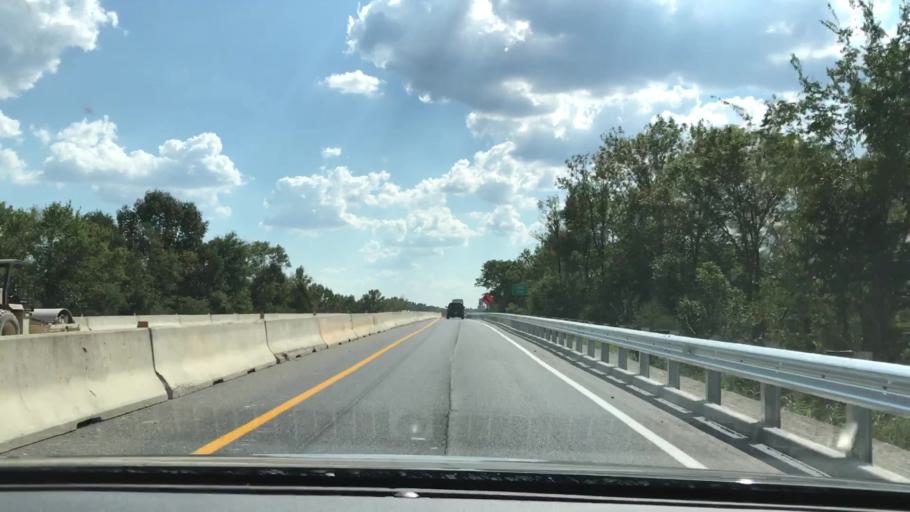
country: US
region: Kentucky
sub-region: Ohio County
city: Oak Grove
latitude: 37.2846
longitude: -86.7430
